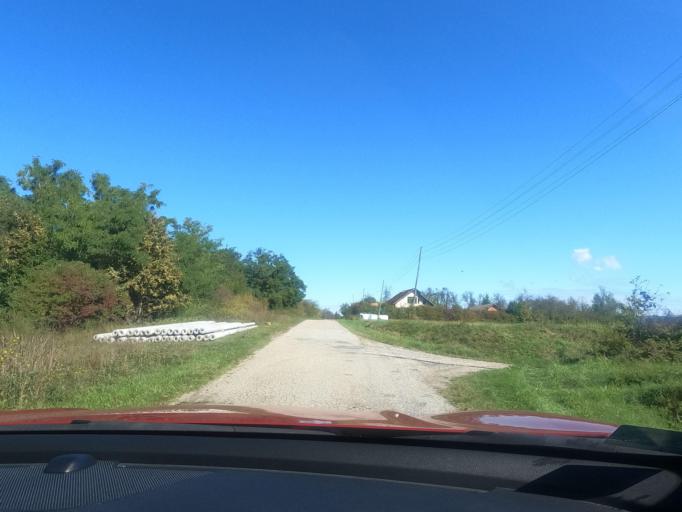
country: HR
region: Sisacko-Moslavacka
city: Petrinja
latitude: 45.3423
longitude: 16.2121
